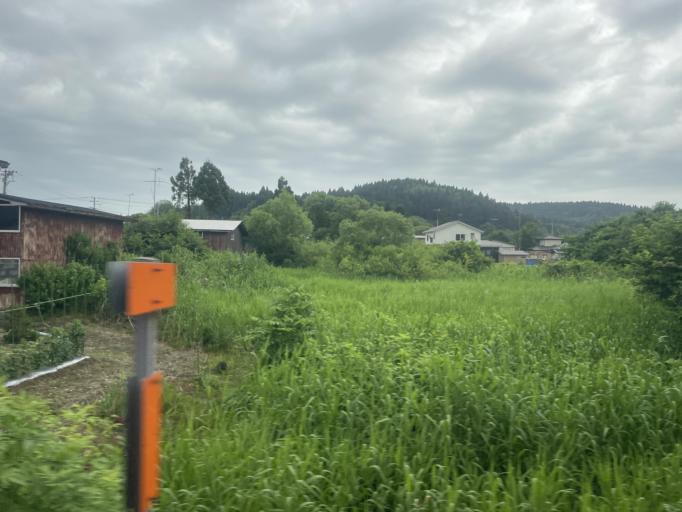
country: JP
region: Akita
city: Tenno
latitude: 39.9160
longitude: 139.8979
